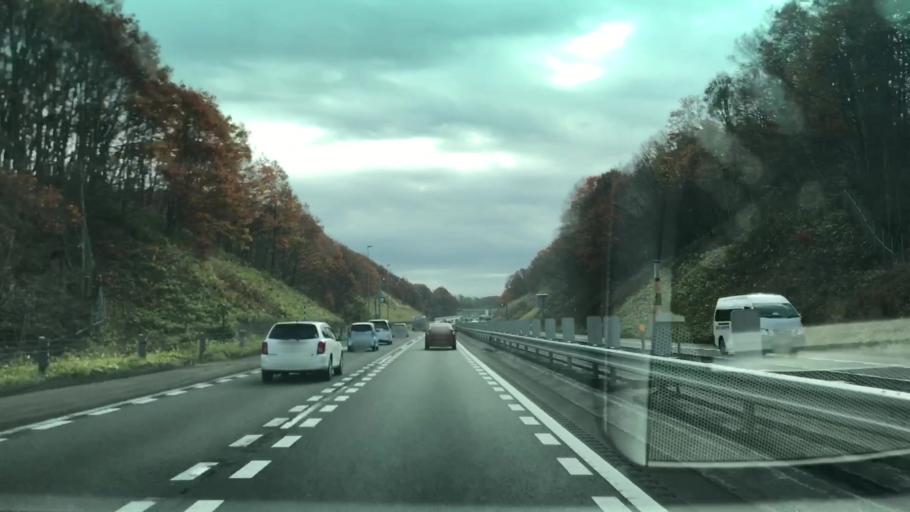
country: JP
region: Hokkaido
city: Kitahiroshima
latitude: 42.9275
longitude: 141.5366
